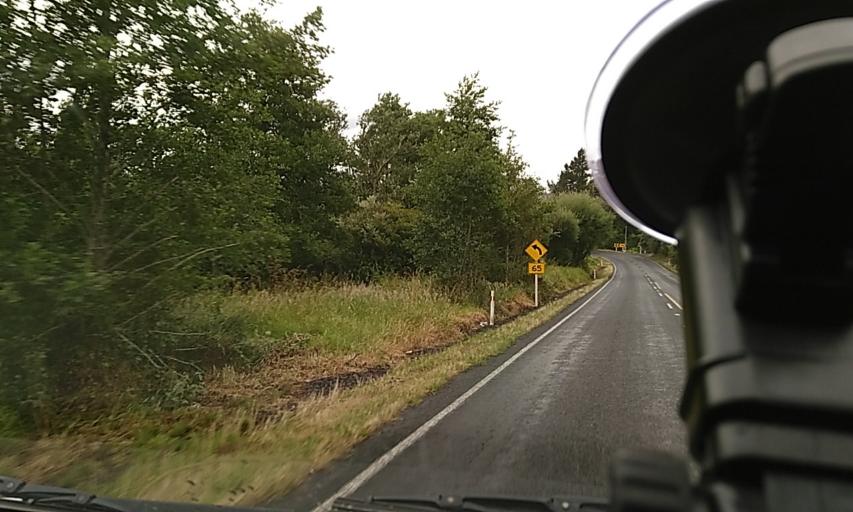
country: NZ
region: Auckland
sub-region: Auckland
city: Pukekohe East
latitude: -37.3003
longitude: 174.9451
